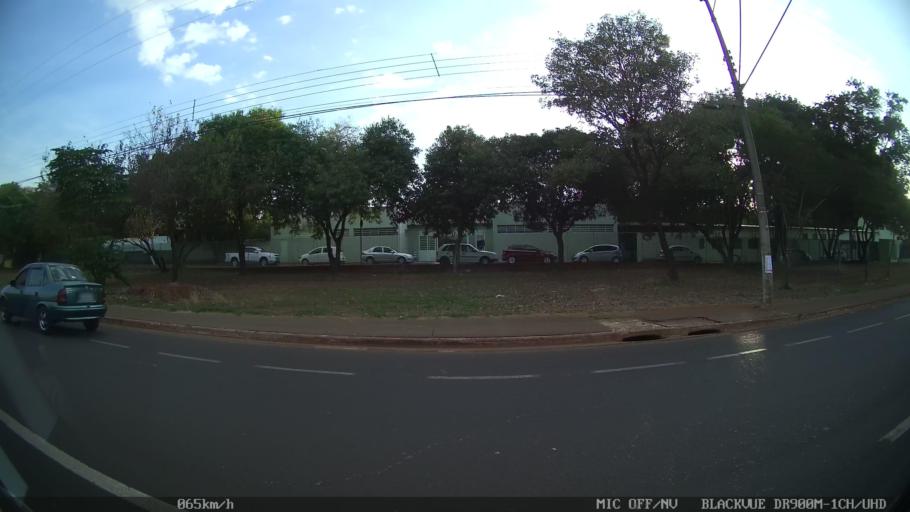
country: BR
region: Sao Paulo
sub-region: Ribeirao Preto
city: Ribeirao Preto
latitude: -21.1390
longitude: -47.8041
